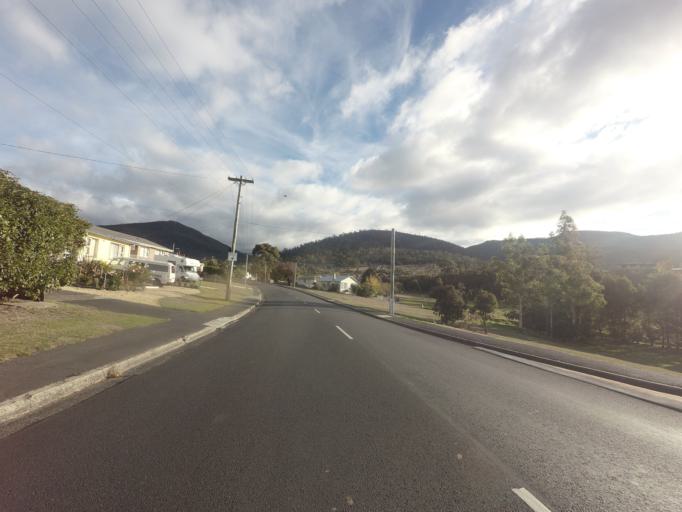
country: AU
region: Tasmania
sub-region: Glenorchy
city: Berriedale
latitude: -42.8037
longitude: 147.2461
